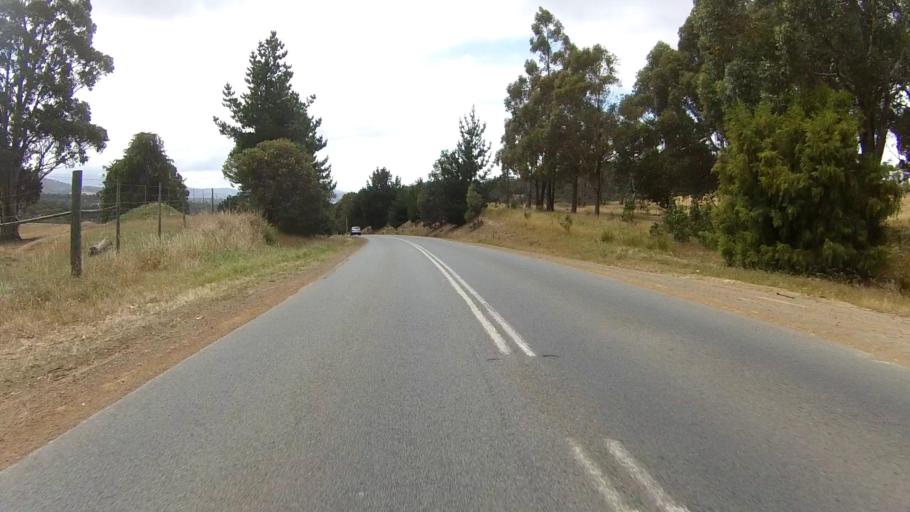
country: AU
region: Tasmania
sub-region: Kingborough
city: Kettering
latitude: -43.0902
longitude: 147.2498
